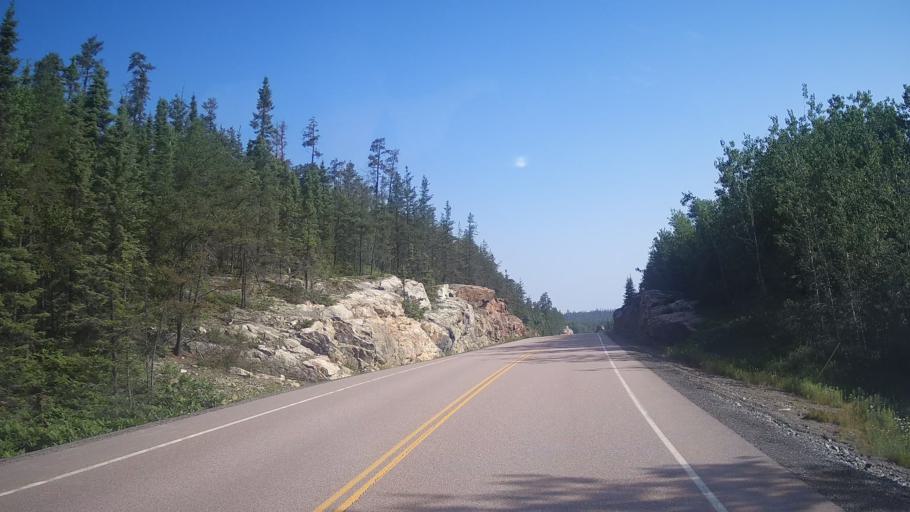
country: CA
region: Ontario
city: Rayside-Balfour
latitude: 46.9834
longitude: -81.6347
